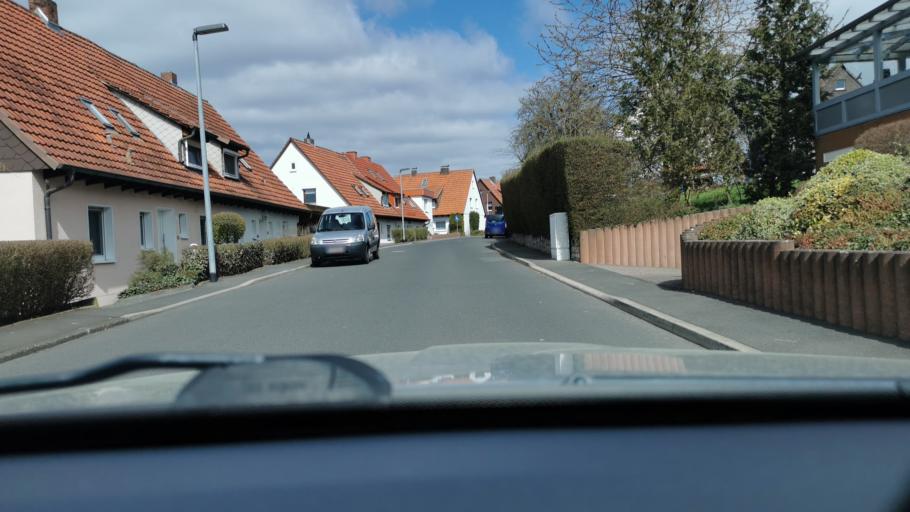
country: DE
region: Hesse
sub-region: Regierungsbezirk Kassel
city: Bad Hersfeld
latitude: 50.8651
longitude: 9.7408
